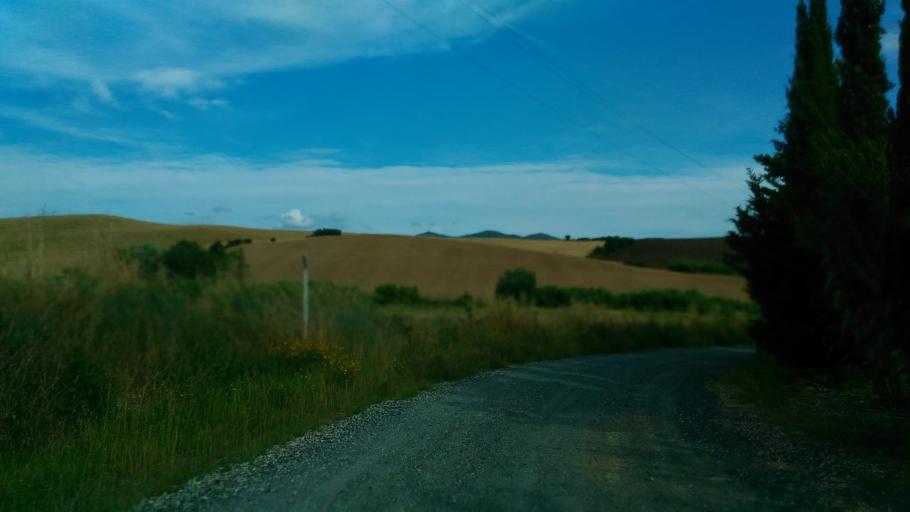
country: IT
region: Tuscany
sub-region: Province of Pisa
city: Orciano Pisano
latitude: 43.4515
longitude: 10.5224
